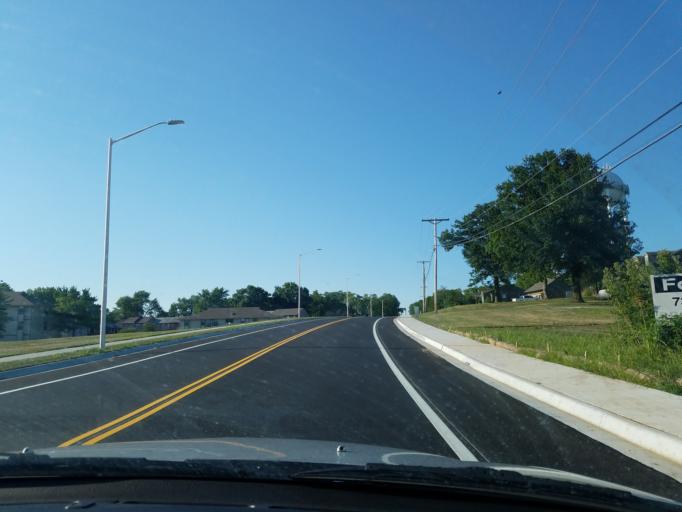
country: US
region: Missouri
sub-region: Clay County
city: Gladstone
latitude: 39.2158
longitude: -94.5353
